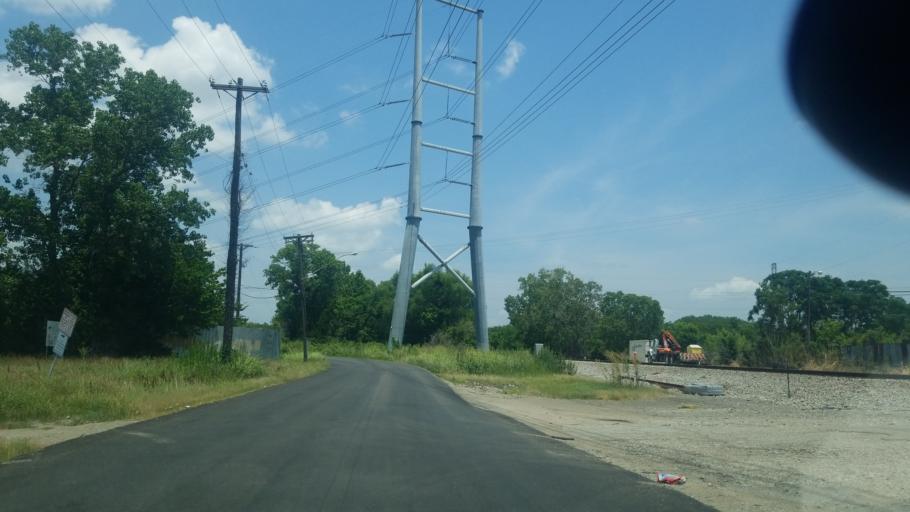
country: US
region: Texas
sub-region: Dallas County
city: Dallas
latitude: 32.7433
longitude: -96.7808
